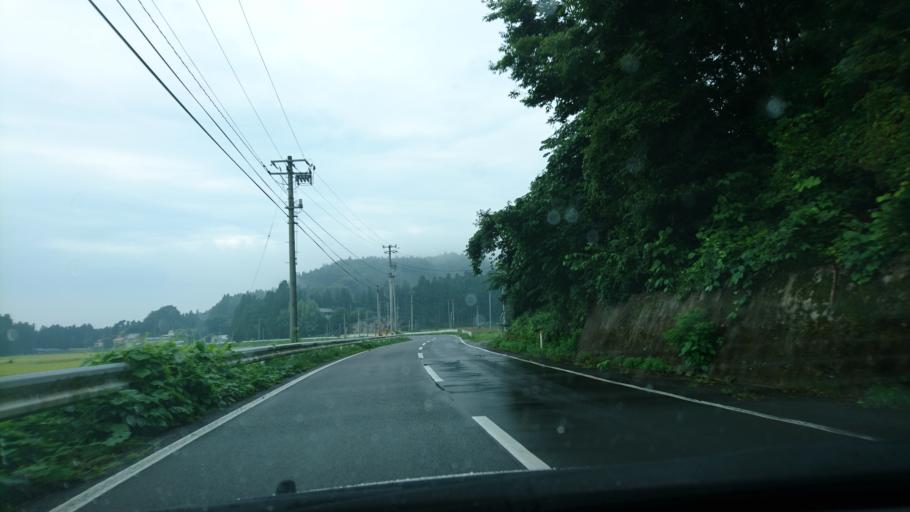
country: JP
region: Iwate
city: Ichinoseki
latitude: 38.8754
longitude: 141.2651
